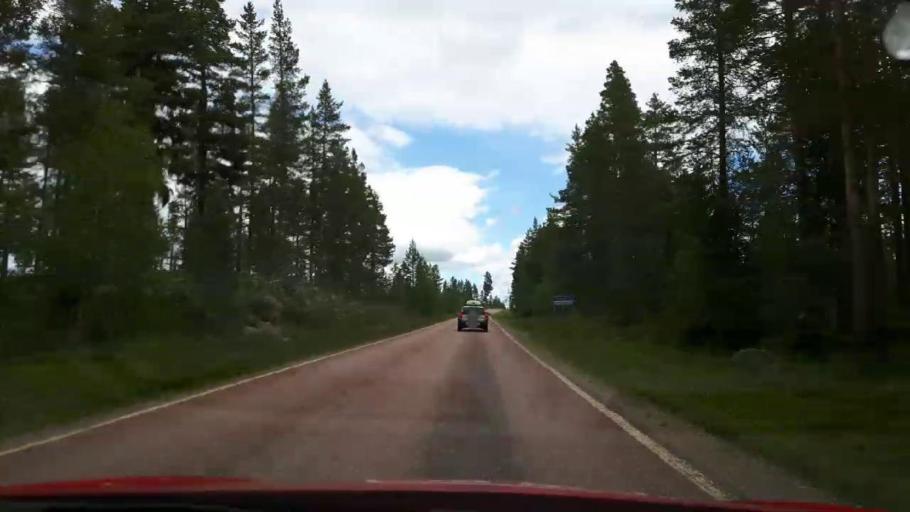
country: NO
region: Hedmark
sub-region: Trysil
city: Innbygda
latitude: 61.8666
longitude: 12.9548
